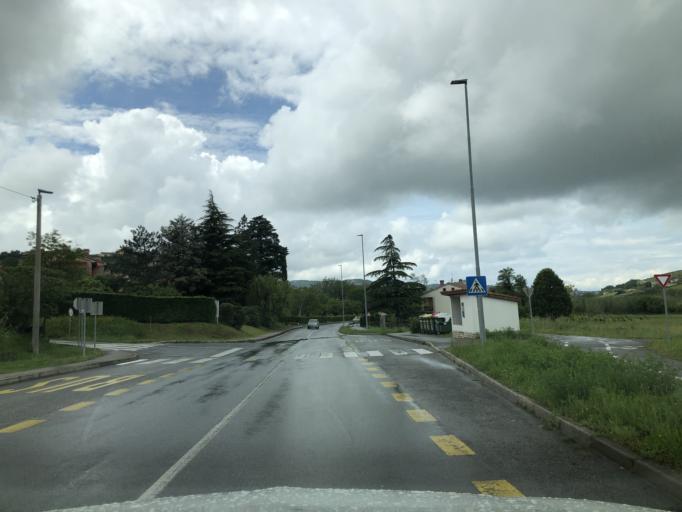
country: SI
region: Koper-Capodistria
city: Prade
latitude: 45.5167
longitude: 13.7651
